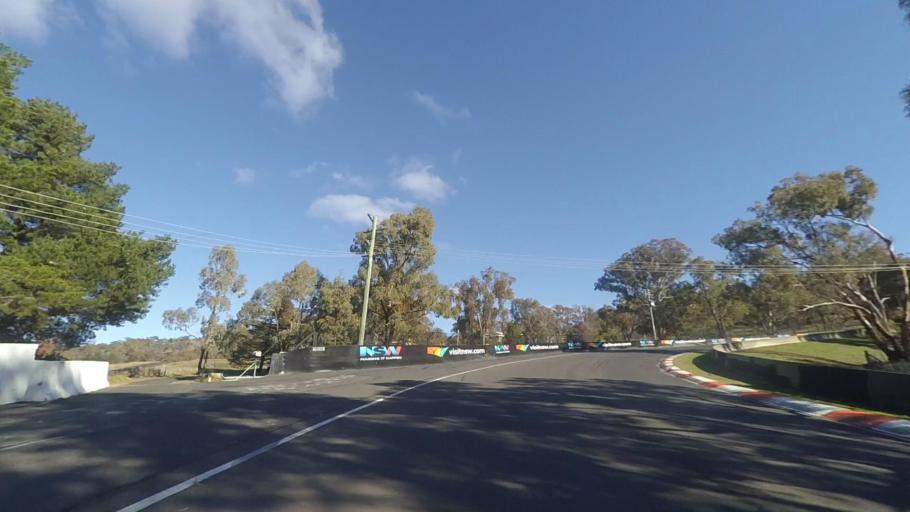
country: AU
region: New South Wales
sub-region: Bathurst Regional
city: Perthville
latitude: -33.4488
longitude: 149.5537
